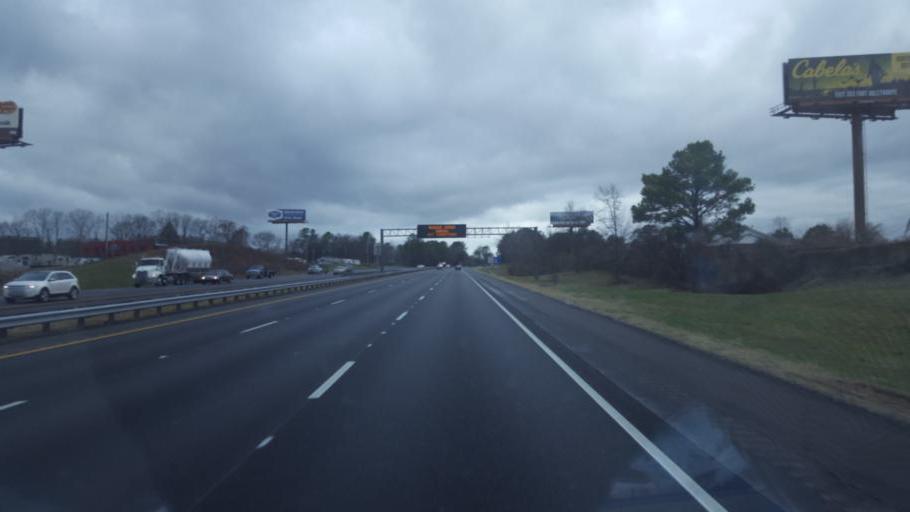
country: US
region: Georgia
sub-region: Catoosa County
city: Ringgold
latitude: 34.9120
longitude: -85.1348
